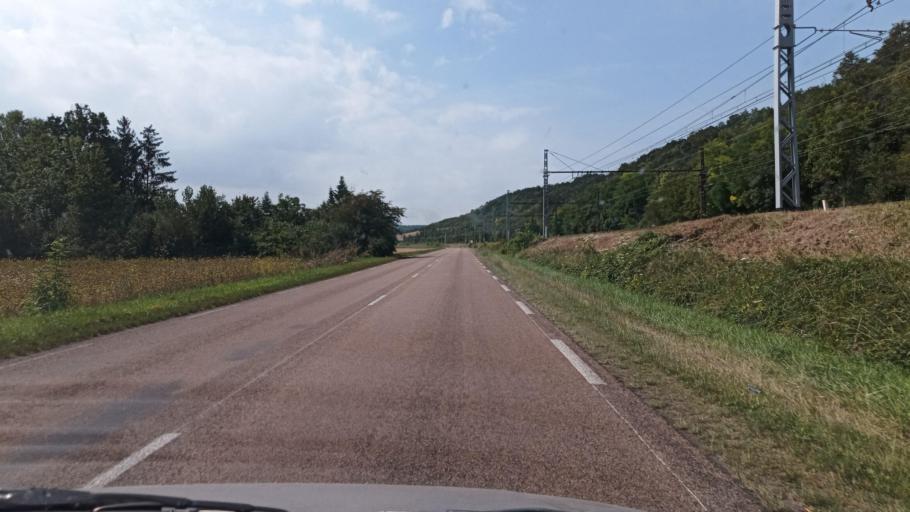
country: FR
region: Bourgogne
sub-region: Departement de l'Yonne
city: Veron
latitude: 48.1281
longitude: 3.2838
